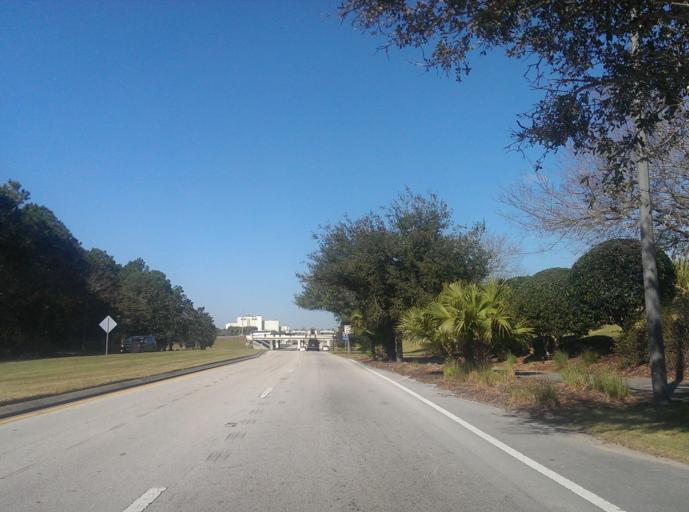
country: US
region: Florida
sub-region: Polk County
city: Loughman
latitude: 28.2604
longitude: -81.6096
